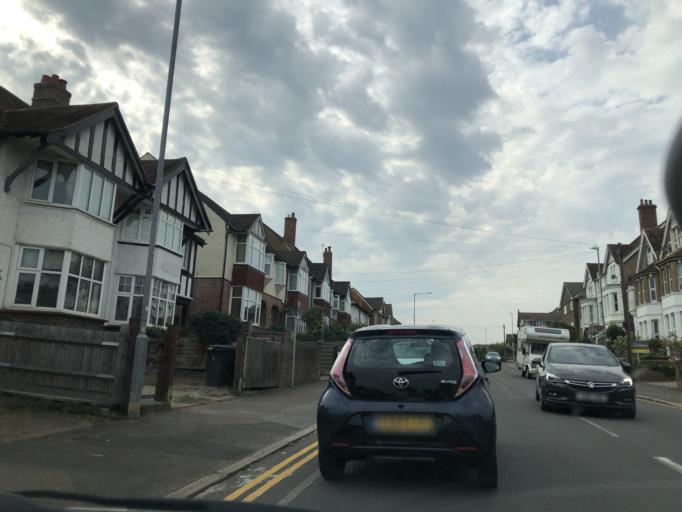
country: GB
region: England
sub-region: East Sussex
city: Bexhill-on-Sea
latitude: 50.8421
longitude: 0.4826
